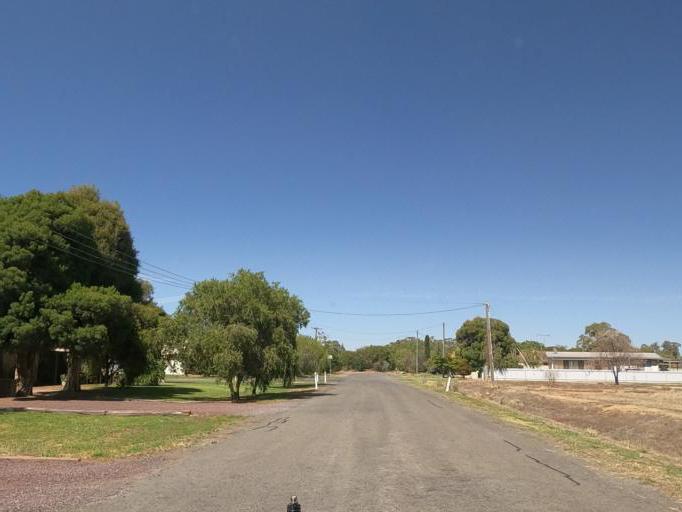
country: AU
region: New South Wales
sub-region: Corowa Shire
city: Mulwala
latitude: -35.9844
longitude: 146.0025
